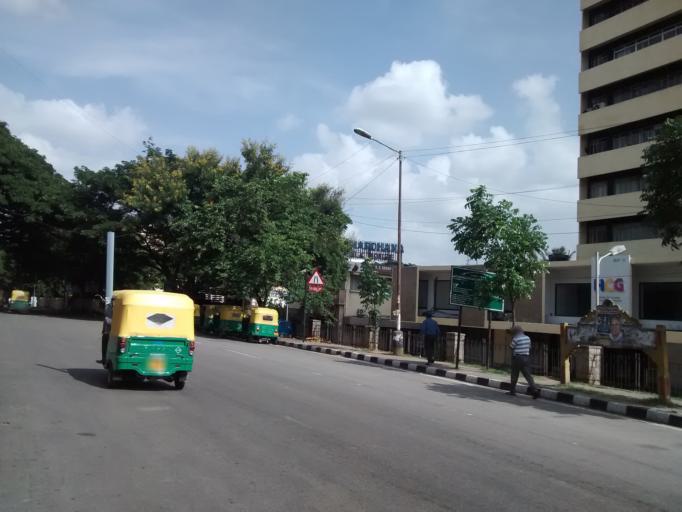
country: IN
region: Karnataka
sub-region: Bangalore Urban
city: Bangalore
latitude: 12.9654
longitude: 77.5870
